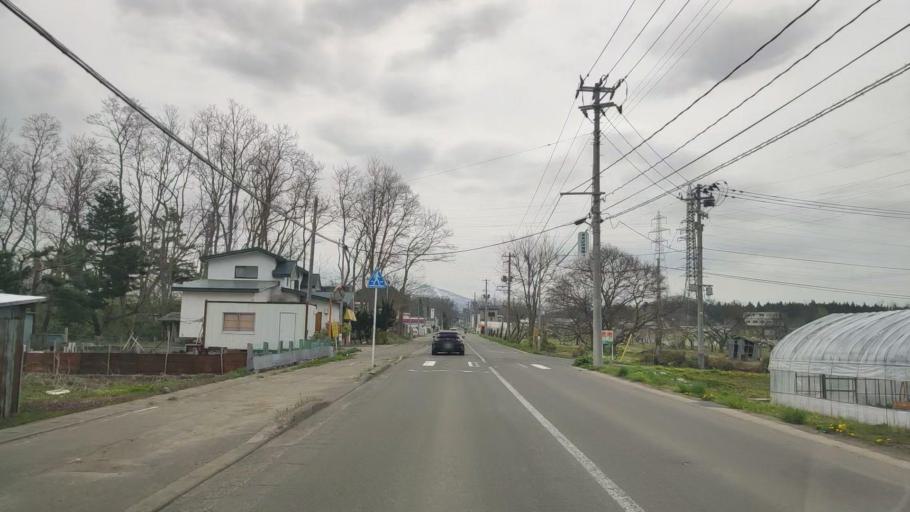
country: JP
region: Aomori
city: Aomori Shi
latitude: 40.7798
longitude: 140.7930
